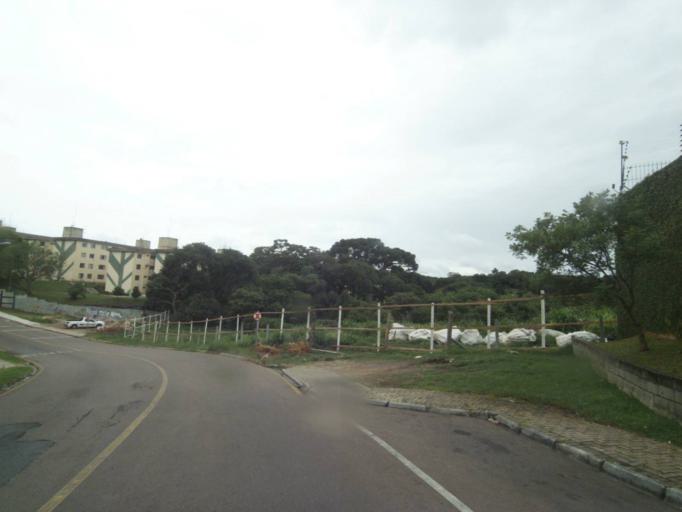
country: BR
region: Parana
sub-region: Curitiba
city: Curitiba
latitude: -25.4619
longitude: -49.3340
